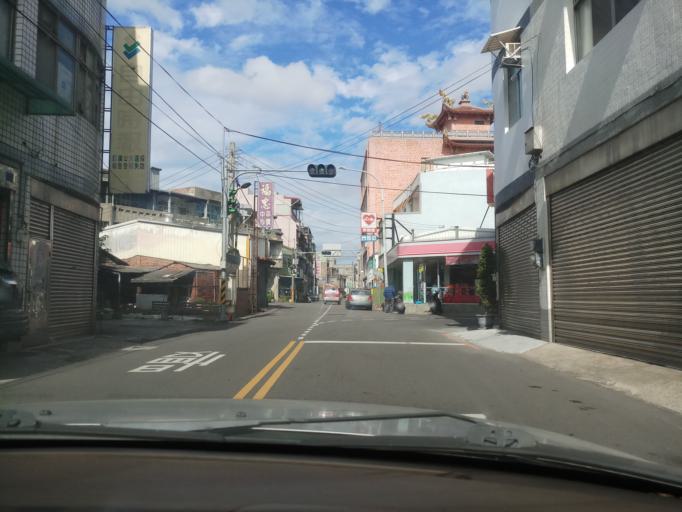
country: TW
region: Taiwan
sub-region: Miaoli
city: Miaoli
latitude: 24.6819
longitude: 120.8629
